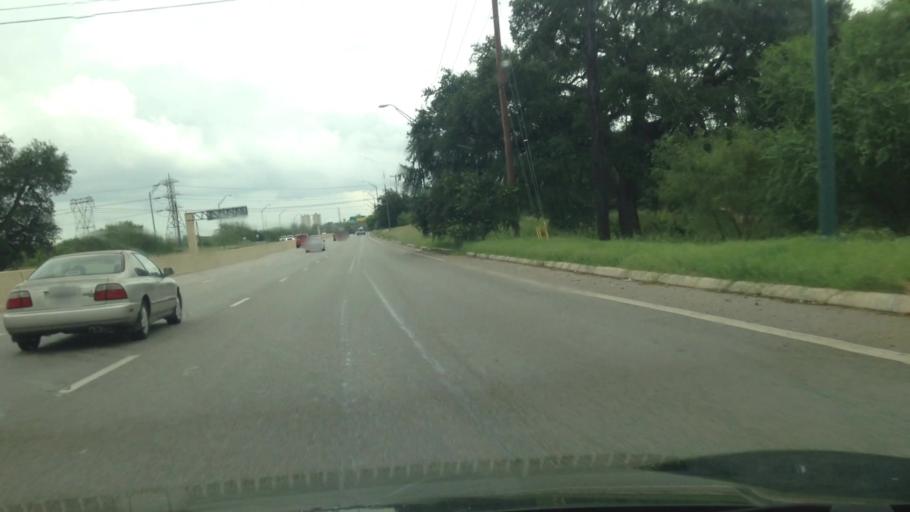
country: US
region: Texas
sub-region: Bexar County
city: Alamo Heights
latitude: 29.5469
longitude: -98.4489
